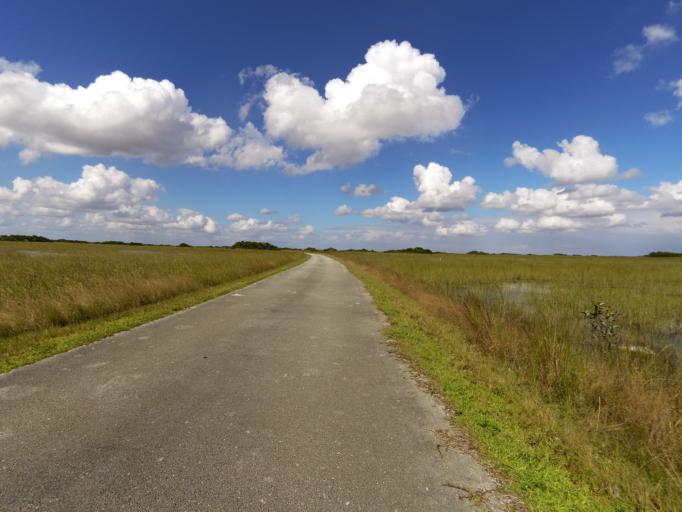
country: US
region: Florida
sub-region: Miami-Dade County
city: The Hammocks
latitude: 25.6823
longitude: -80.7625
